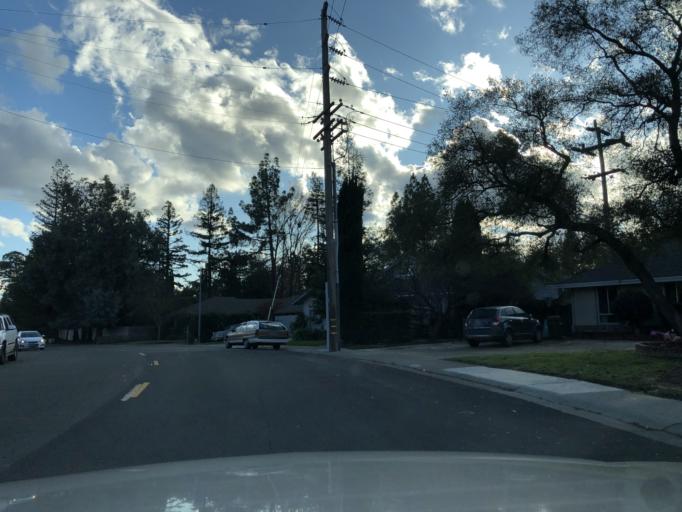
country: US
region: California
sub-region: Sacramento County
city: Foothill Farms
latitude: 38.6565
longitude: -121.3324
